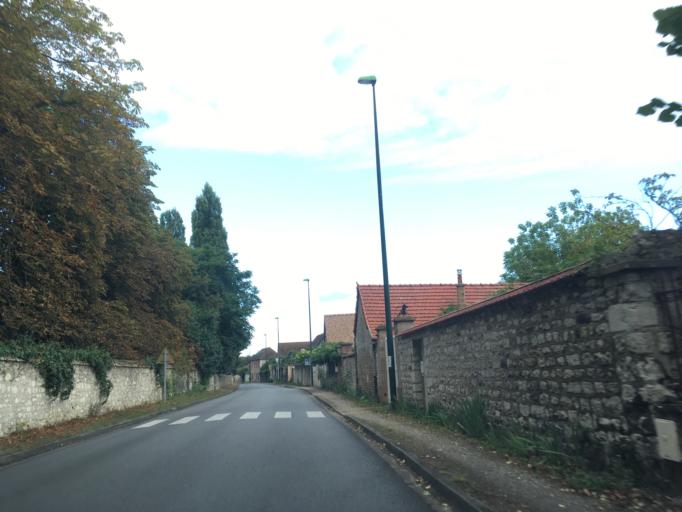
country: FR
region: Haute-Normandie
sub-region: Departement de l'Eure
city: Saint-Just
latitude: 49.1303
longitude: 1.4478
